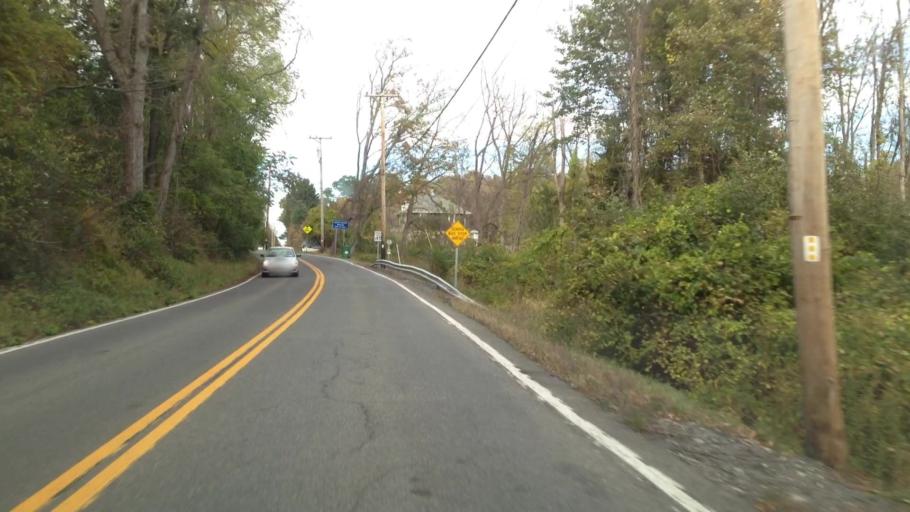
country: US
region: New York
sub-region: Ulster County
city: Rosendale Village
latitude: 41.8635
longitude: -74.0308
